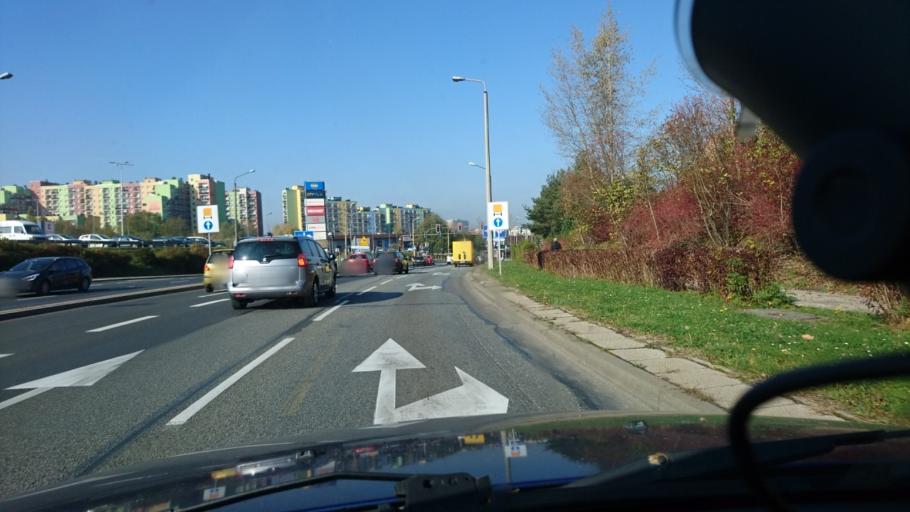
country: PL
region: Silesian Voivodeship
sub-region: Bielsko-Biala
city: Bielsko-Biala
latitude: 49.8012
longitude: 19.0326
